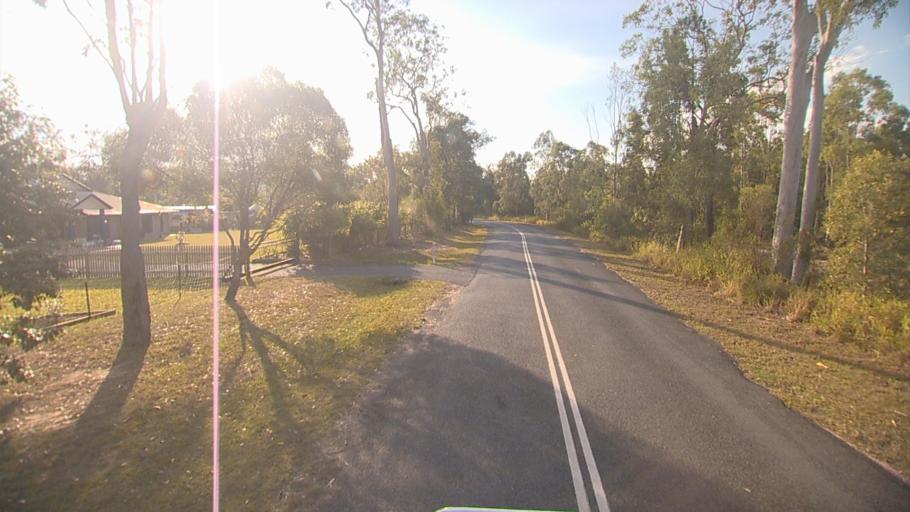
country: AU
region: Queensland
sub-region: Logan
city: Chambers Flat
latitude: -27.8404
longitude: 153.1191
